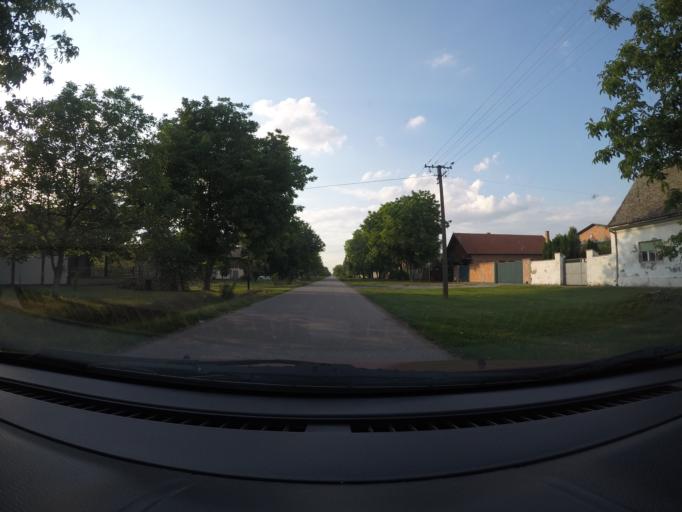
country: RS
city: Debeljaca
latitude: 45.0678
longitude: 20.6070
